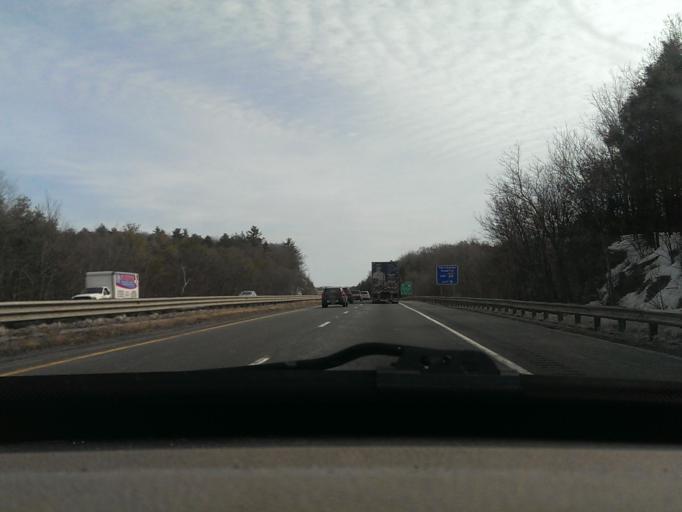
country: US
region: Massachusetts
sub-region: Worcester County
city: Sturbridge
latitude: 42.1336
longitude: -72.0766
